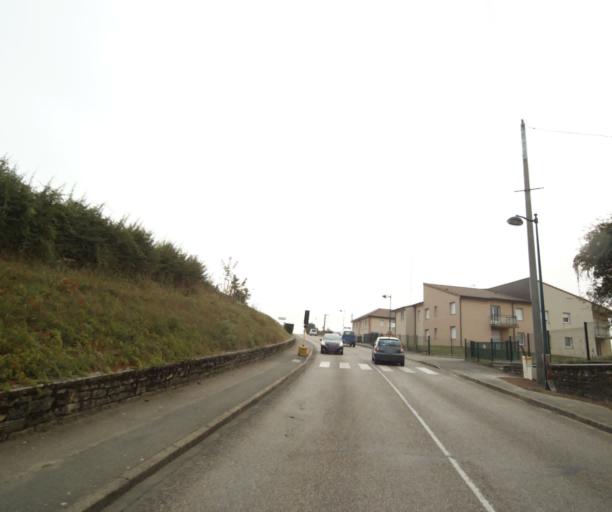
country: FR
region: Bourgogne
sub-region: Departement de Saone-et-Loire
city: Charolles
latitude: 46.4372
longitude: 4.2826
